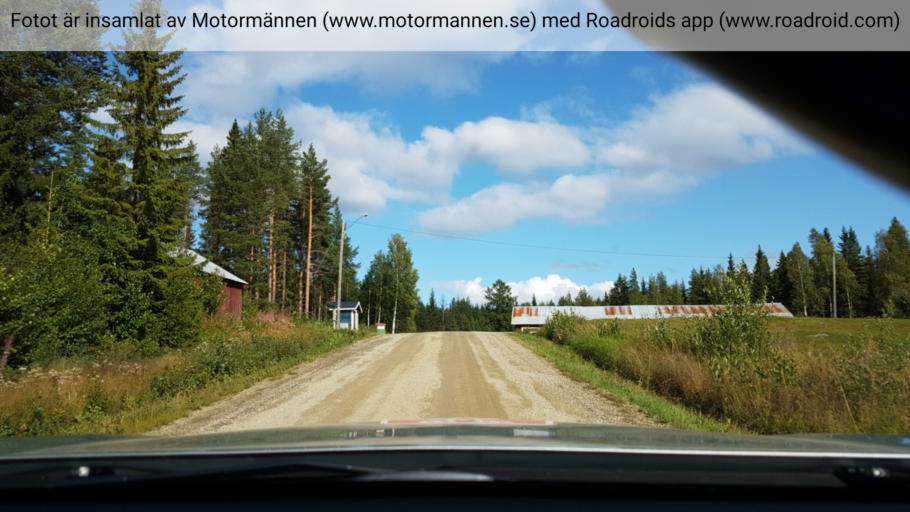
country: SE
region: Vaesterbotten
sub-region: Lycksele Kommun
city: Lycksele
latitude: 64.5799
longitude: 19.0384
